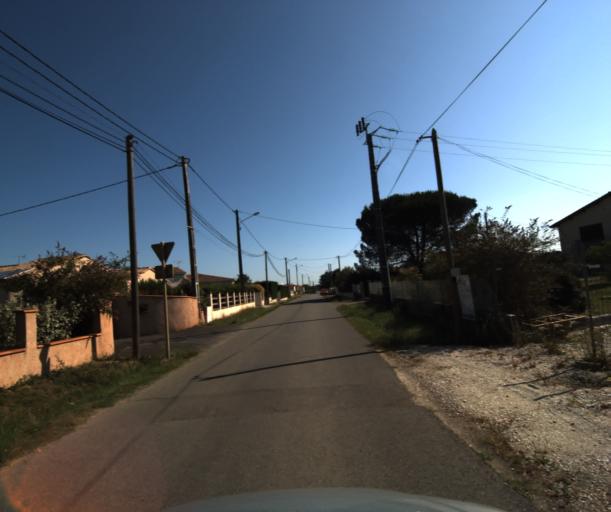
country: FR
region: Midi-Pyrenees
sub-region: Departement de la Haute-Garonne
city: Eaunes
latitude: 43.4317
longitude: 1.3623
